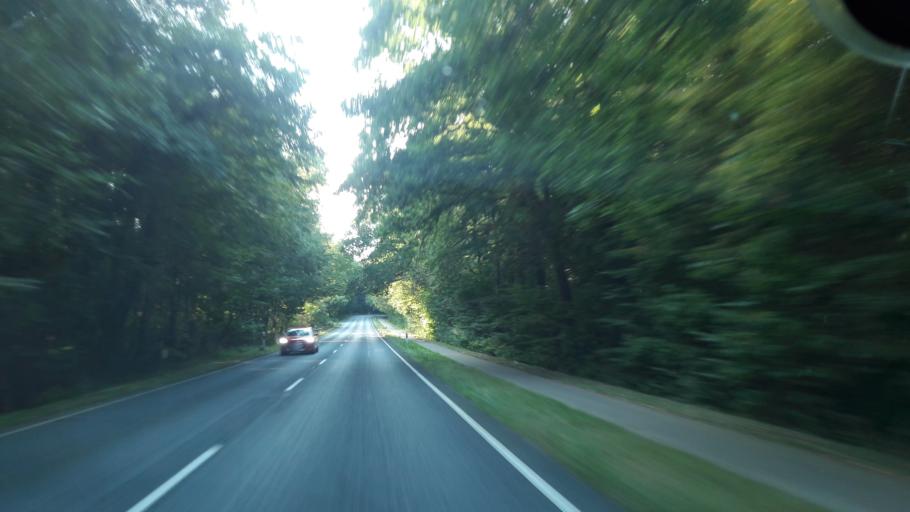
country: DE
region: Lower Saxony
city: Diekholzen
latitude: 52.1199
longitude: 9.8946
